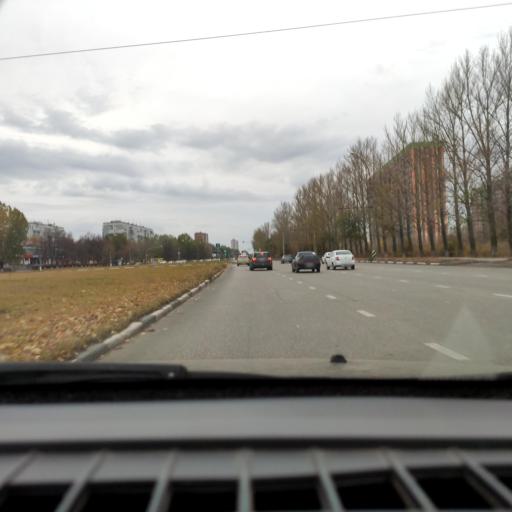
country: RU
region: Samara
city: Tol'yatti
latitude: 53.5212
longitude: 49.2587
